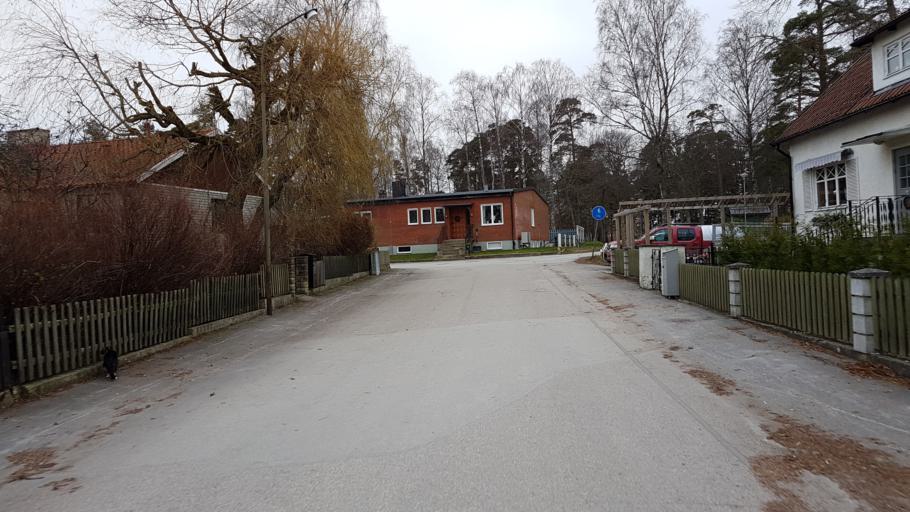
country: SE
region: Gotland
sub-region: Gotland
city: Visby
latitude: 57.6214
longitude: 18.3060
